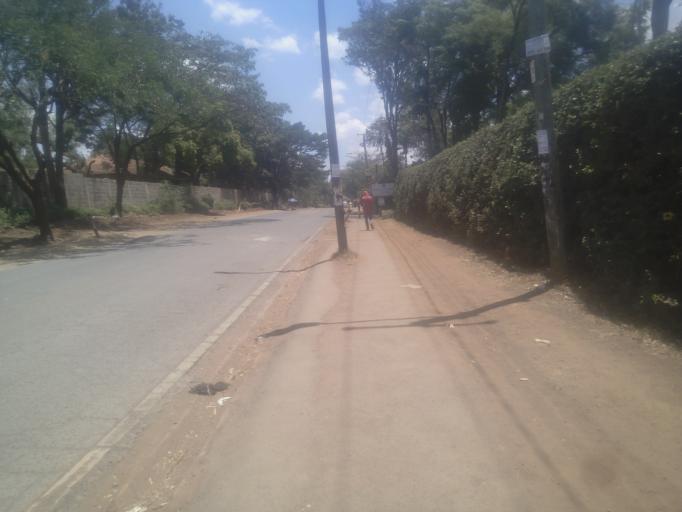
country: KE
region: Nairobi Area
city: Nairobi
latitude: -1.3037
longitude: 36.7821
